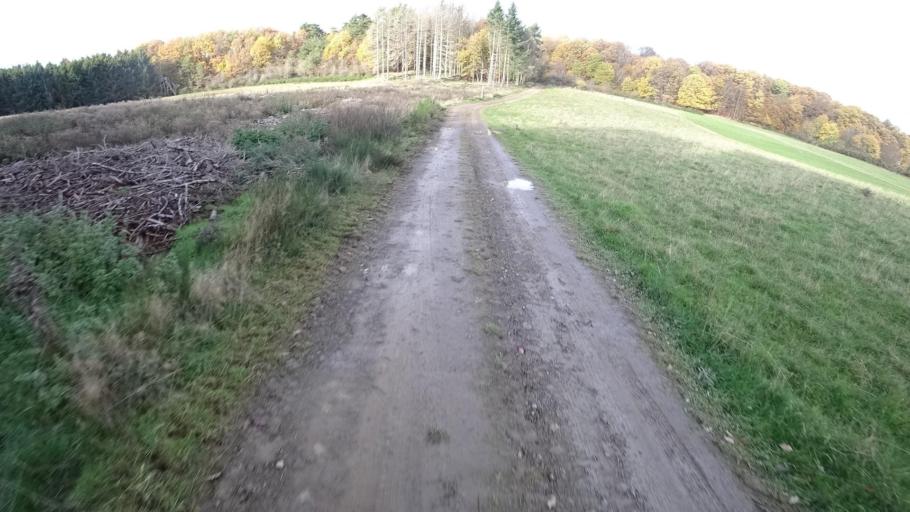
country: DE
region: Rheinland-Pfalz
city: Honningen
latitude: 50.4776
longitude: 6.9382
